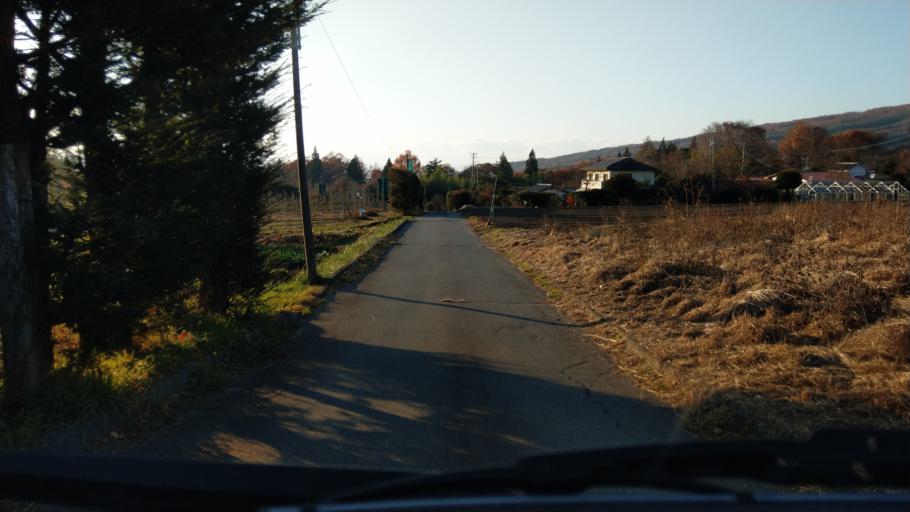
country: JP
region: Nagano
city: Komoro
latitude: 36.3524
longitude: 138.4497
